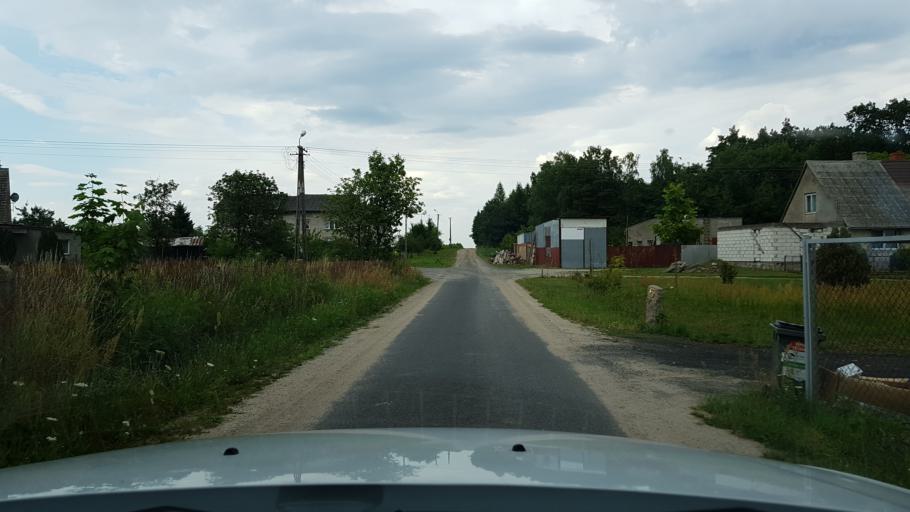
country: PL
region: West Pomeranian Voivodeship
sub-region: Powiat walecki
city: Walcz
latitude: 53.3685
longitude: 16.3402
